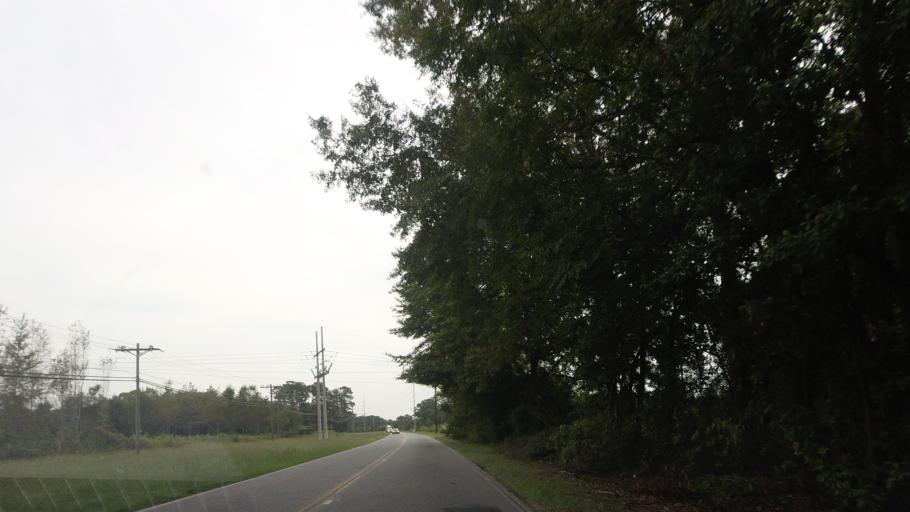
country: US
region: Georgia
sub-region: Houston County
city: Robins Air Force Base
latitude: 32.5911
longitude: -83.6058
